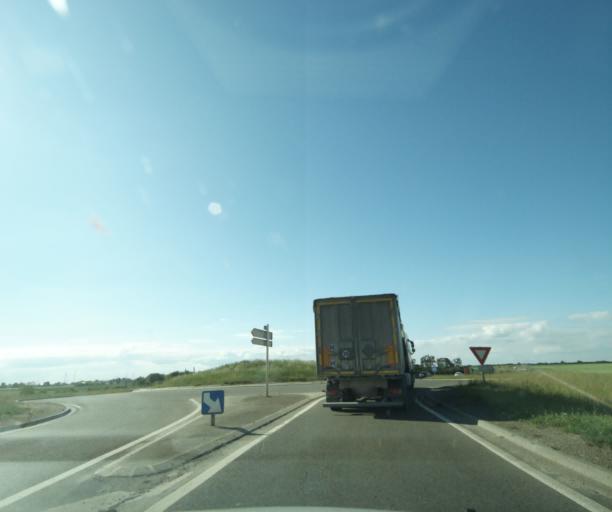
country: FR
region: Centre
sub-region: Departement d'Eure-et-Loir
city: Janville
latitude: 48.2544
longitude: 1.7640
